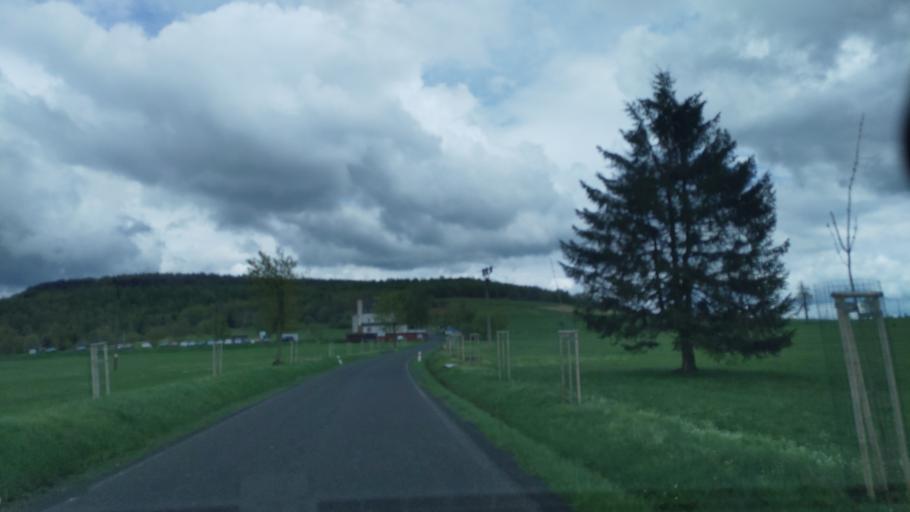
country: CZ
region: Ustecky
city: Jilove
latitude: 50.7916
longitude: 14.0837
